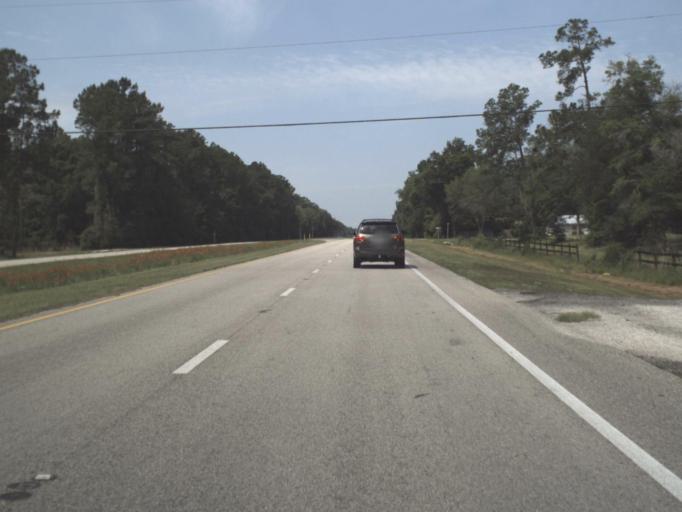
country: US
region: Florida
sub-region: Alachua County
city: Waldo
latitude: 29.7425
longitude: -82.2326
